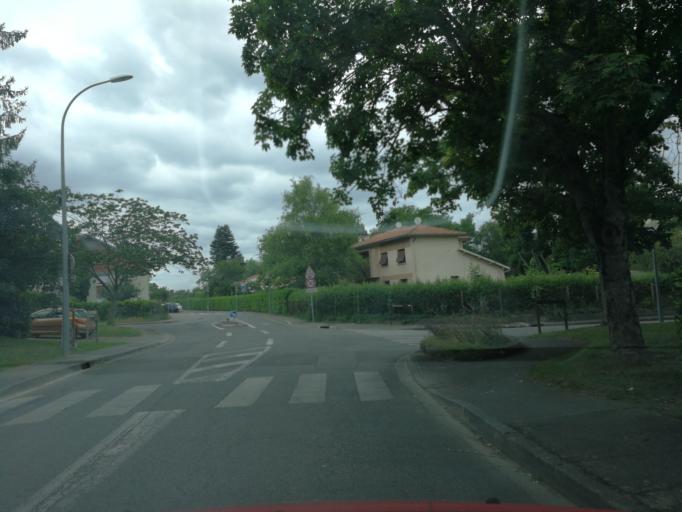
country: FR
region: Midi-Pyrenees
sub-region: Departement de la Haute-Garonne
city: Auzeville-Tolosane
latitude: 43.5279
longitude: 1.4819
